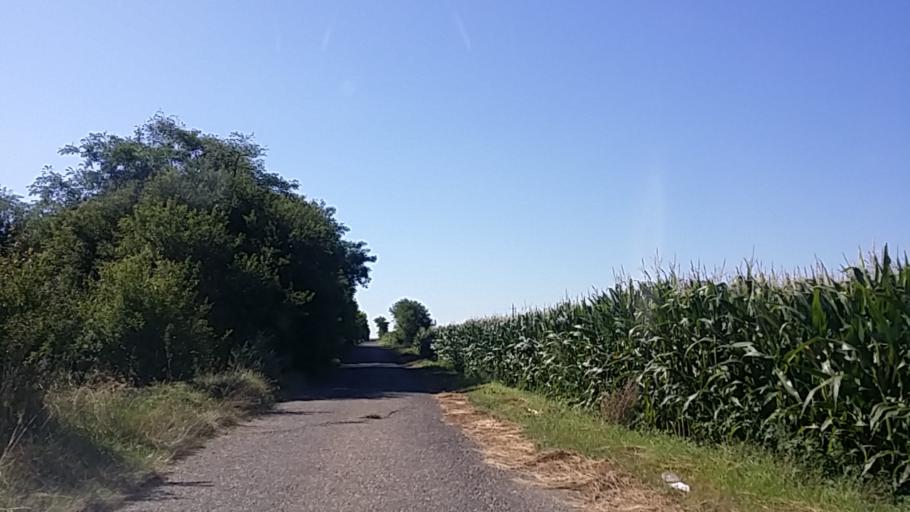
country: HU
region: Fejer
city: Mezofalva
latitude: 46.8941
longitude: 18.7096
